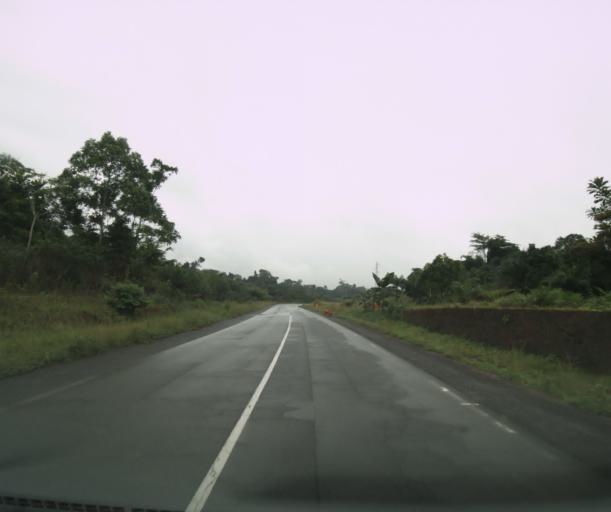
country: CM
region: Littoral
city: Dizangue
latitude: 3.3729
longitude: 10.1029
